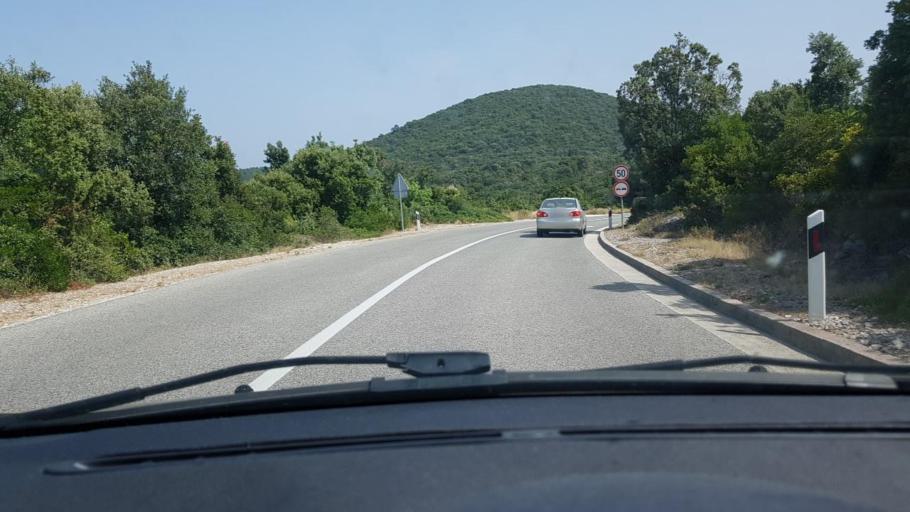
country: HR
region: Dubrovacko-Neretvanska
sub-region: Grad Korcula
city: Zrnovo
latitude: 42.9434
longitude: 17.0525
